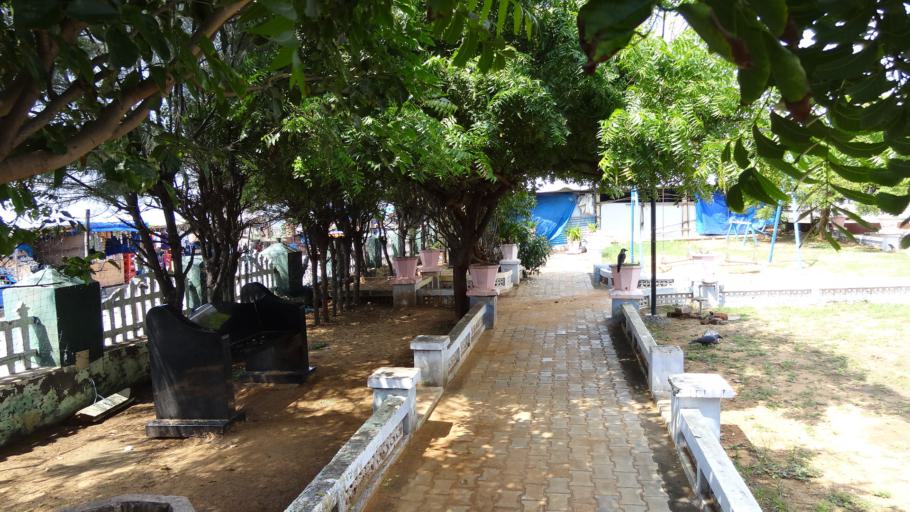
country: IN
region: Tamil Nadu
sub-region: Kanniyakumari
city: Kanniyakumari
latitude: 8.0793
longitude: 77.5482
